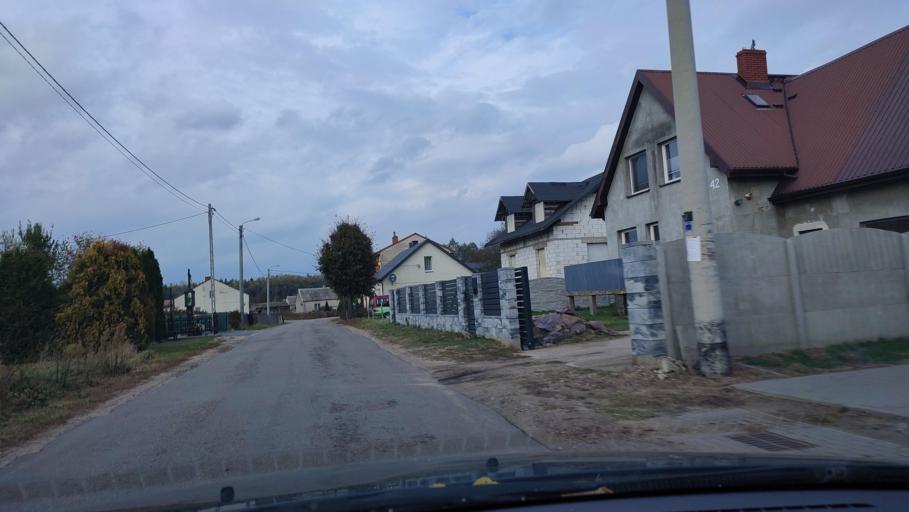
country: PL
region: Masovian Voivodeship
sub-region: Powiat mlawski
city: Mlawa
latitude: 53.1705
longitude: 20.3640
